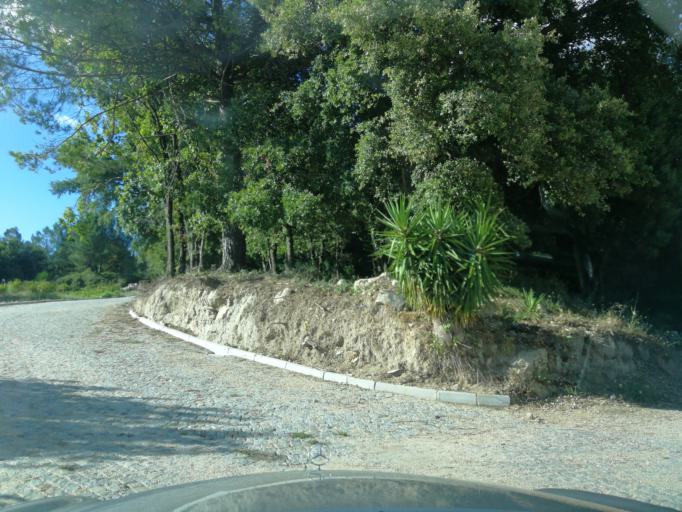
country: PT
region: Braga
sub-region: Braga
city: Adaufe
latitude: 41.5735
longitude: -8.3807
